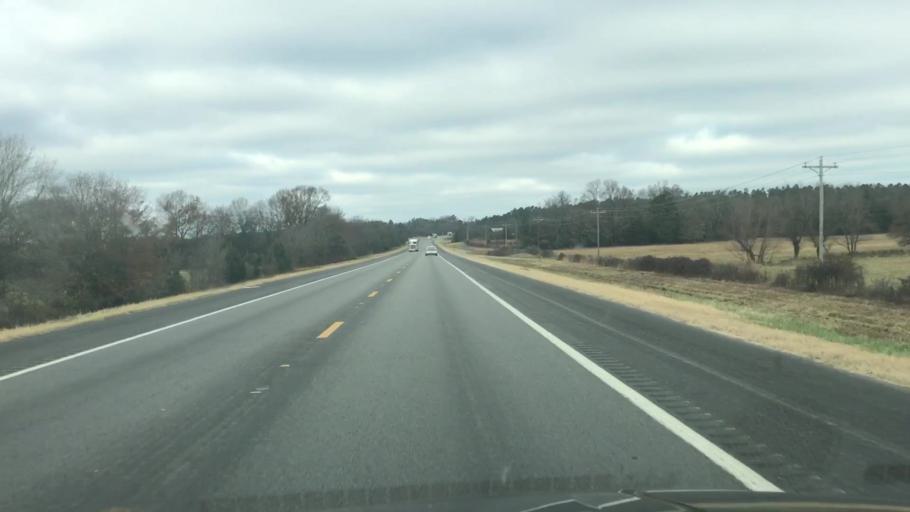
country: US
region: Arkansas
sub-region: Scott County
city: Waldron
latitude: 34.8784
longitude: -94.0972
